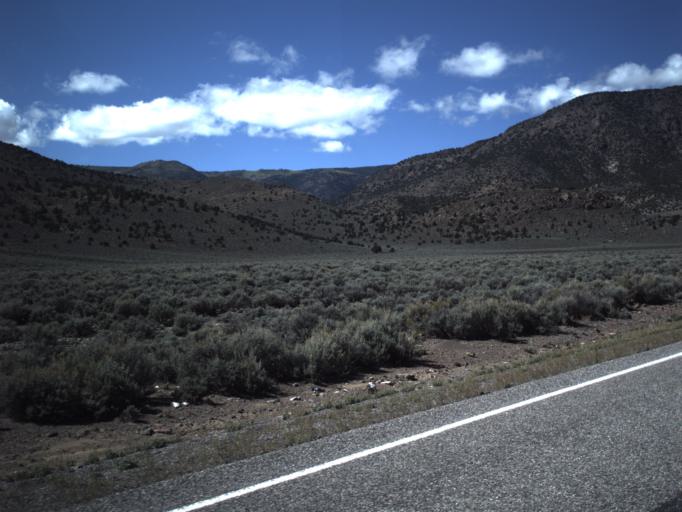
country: US
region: Utah
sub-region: Piute County
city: Junction
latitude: 38.2545
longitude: -112.2430
